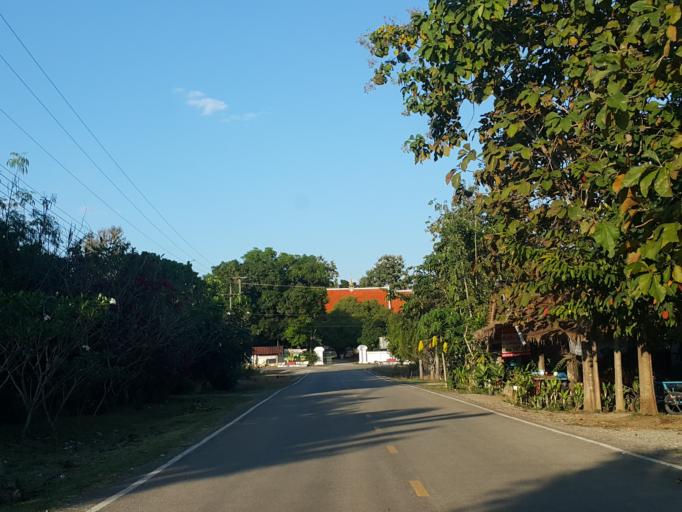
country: TH
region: Lampang
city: Lampang
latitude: 18.4181
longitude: 99.5517
